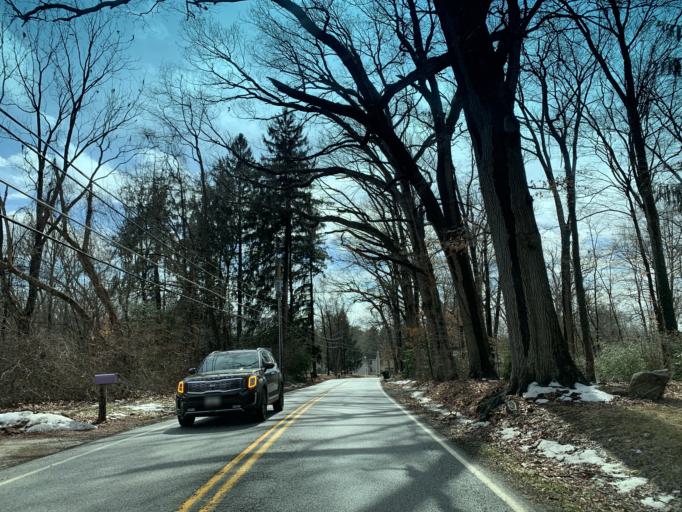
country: US
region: Delaware
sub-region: New Castle County
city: Newark
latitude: 39.7105
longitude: -75.8004
